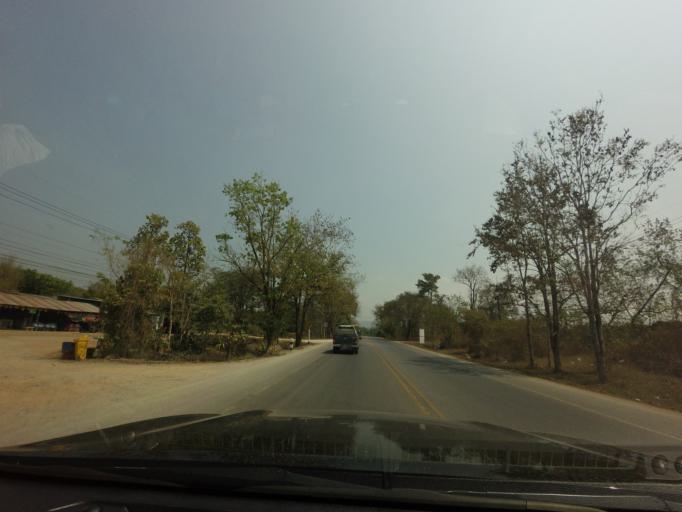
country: TH
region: Kanchanaburi
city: Thong Pha Phum
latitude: 14.6437
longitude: 98.6942
